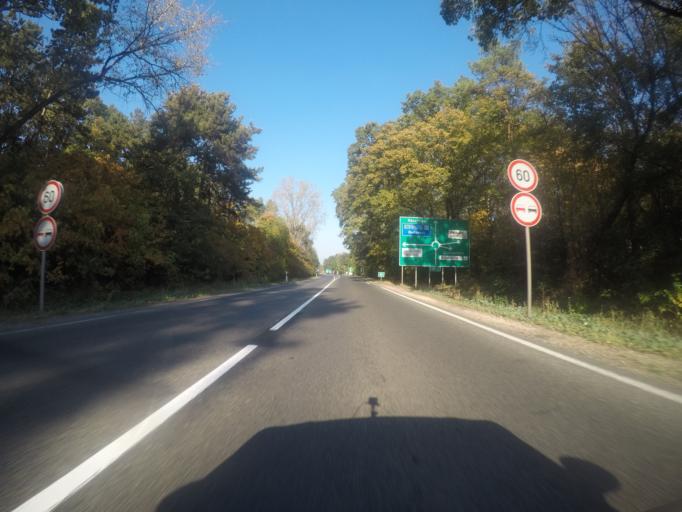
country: HU
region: Fejer
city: dunaujvaros
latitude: 46.9953
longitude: 18.9276
